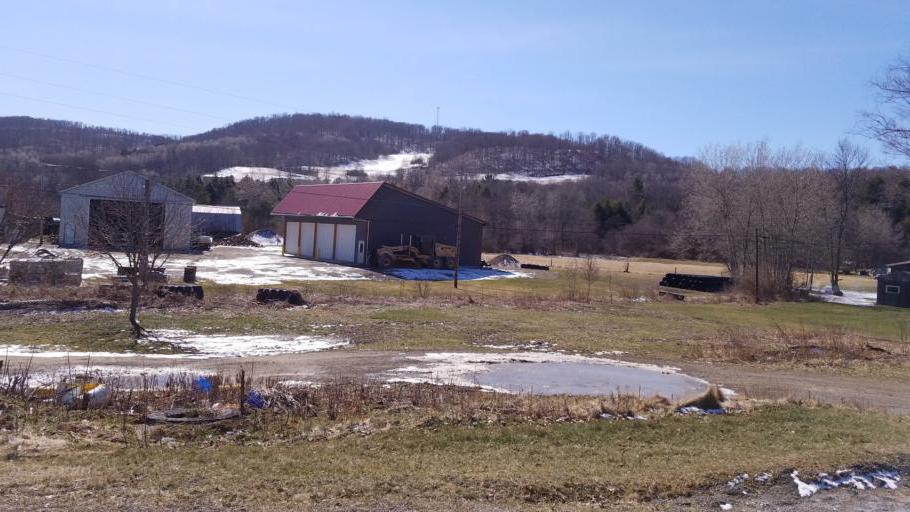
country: US
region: New York
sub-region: Allegany County
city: Wellsville
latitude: 41.9860
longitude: -77.8614
